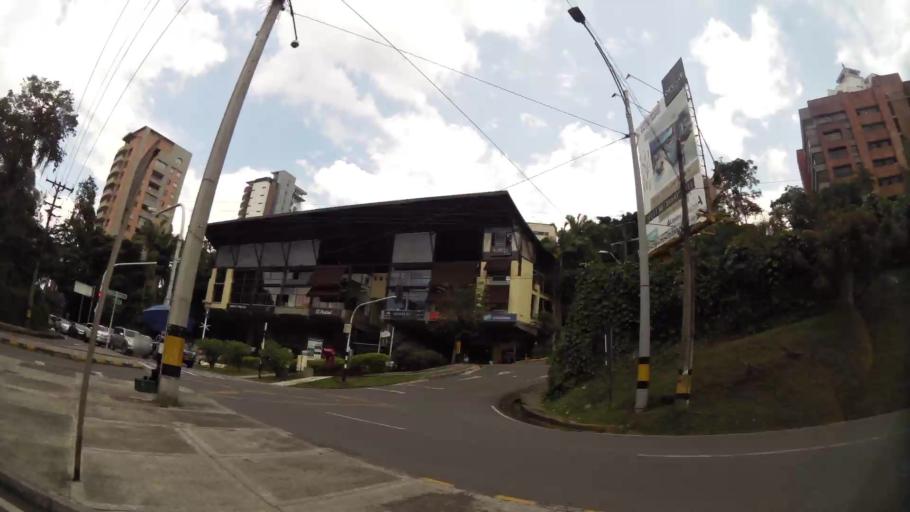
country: CO
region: Antioquia
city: Envigado
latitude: 6.1858
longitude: -75.5700
